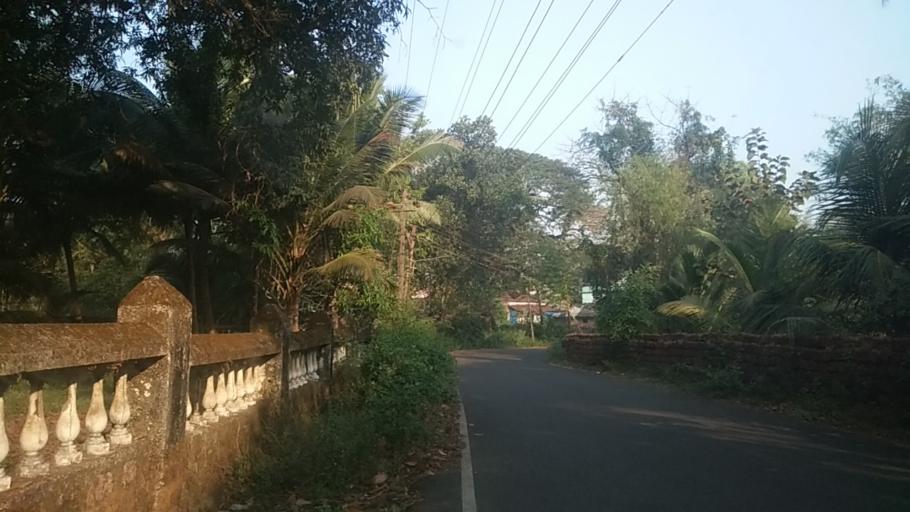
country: IN
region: Goa
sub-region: South Goa
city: Chinchinim
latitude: 15.1991
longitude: 73.9785
